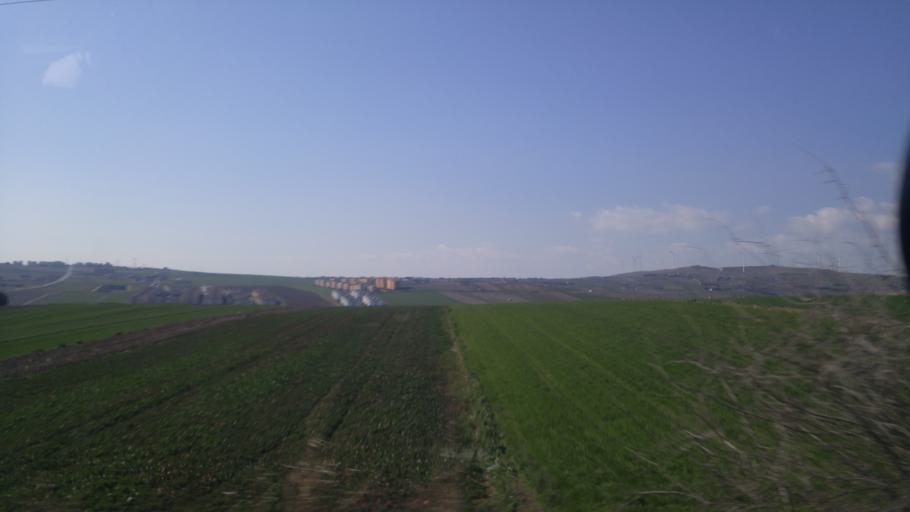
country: TR
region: Istanbul
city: Canta
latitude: 41.0934
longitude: 28.1094
